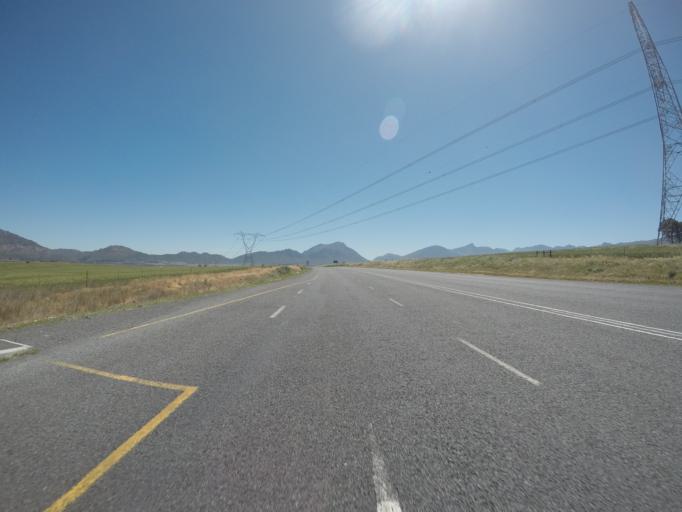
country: ZA
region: Western Cape
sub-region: Cape Winelands District Municipality
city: Ceres
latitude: -33.3305
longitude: 19.1568
